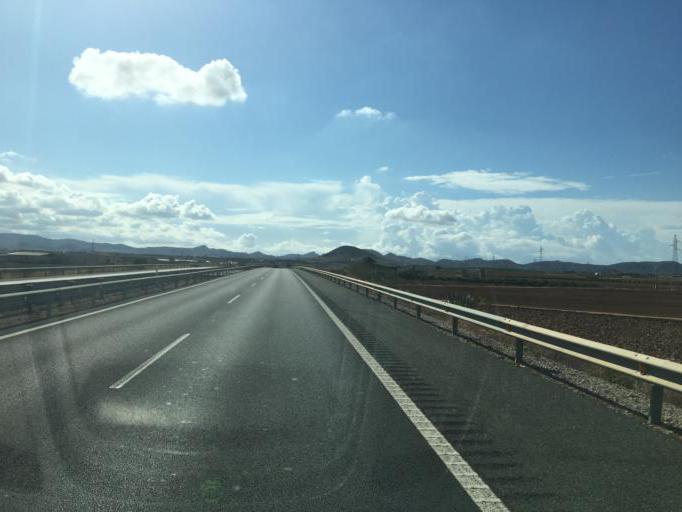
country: ES
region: Murcia
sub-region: Murcia
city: Cartagena
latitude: 37.6502
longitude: -0.9747
